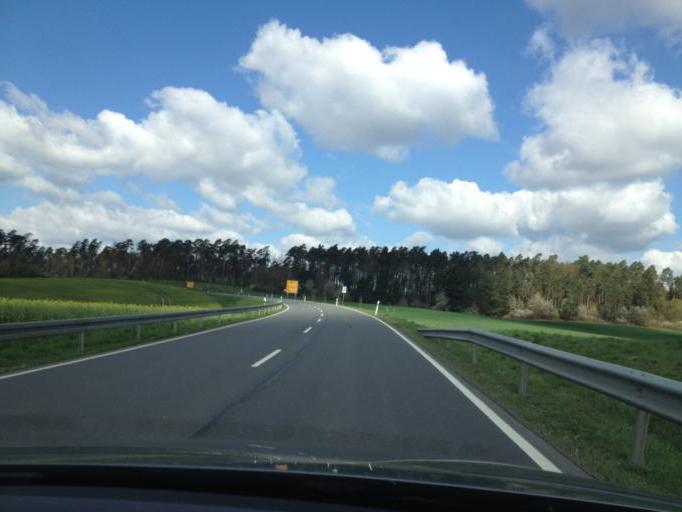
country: DE
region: Baden-Wuerttemberg
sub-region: Karlsruhe Region
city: Osterburken
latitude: 49.4150
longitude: 9.4539
